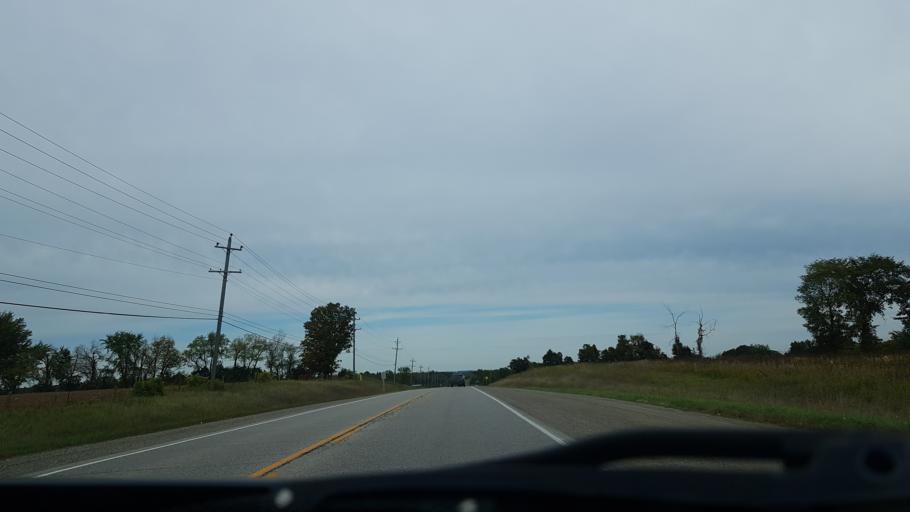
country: CA
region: Ontario
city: Orangeville
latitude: 43.7884
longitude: -80.0750
